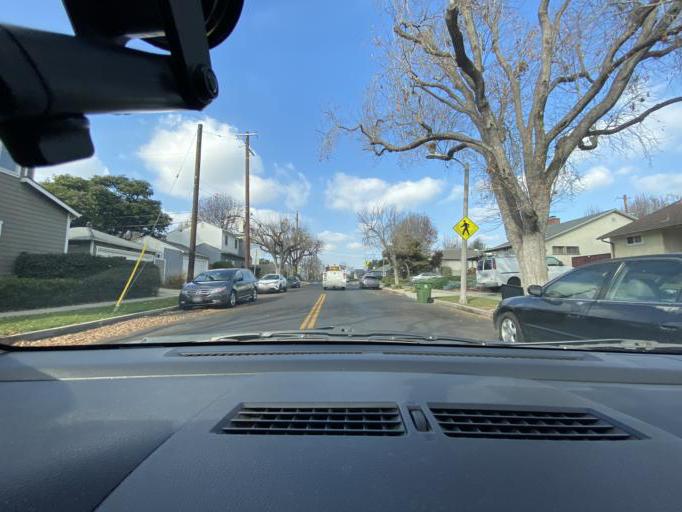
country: US
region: California
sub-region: Los Angeles County
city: Culver City
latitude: 34.0183
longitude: -118.4290
